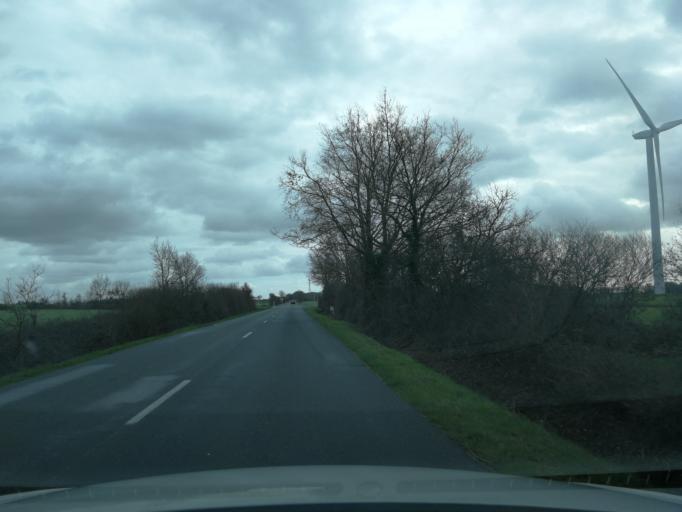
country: FR
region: Pays de la Loire
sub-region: Departement de la Loire-Atlantique
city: La Planche
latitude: 47.0040
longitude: -1.4712
